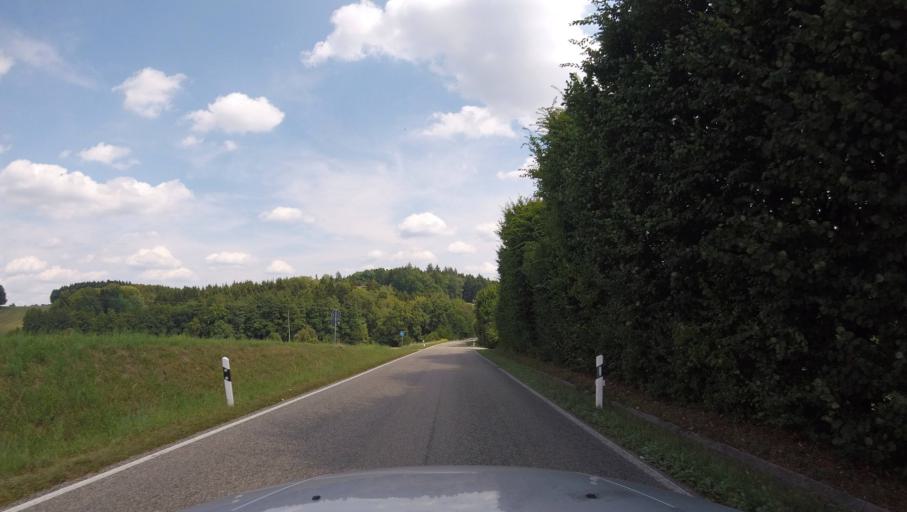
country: DE
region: Baden-Wuerttemberg
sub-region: Regierungsbezirk Stuttgart
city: Kaisersbach
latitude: 48.9272
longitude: 9.6527
